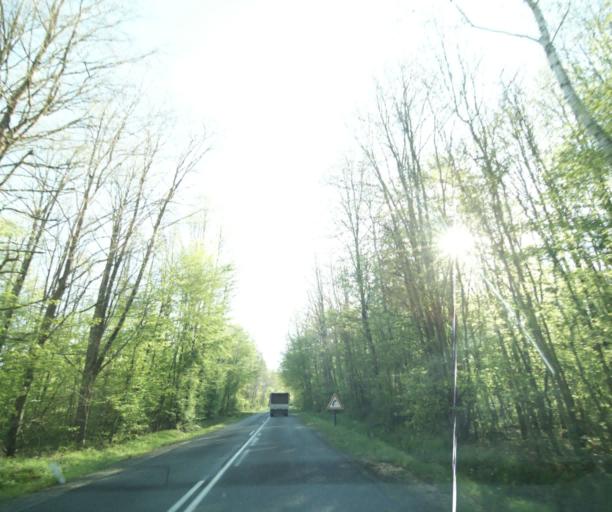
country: FR
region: Ile-de-France
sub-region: Departement de Seine-et-Marne
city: La Chapelle-Gauthier
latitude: 48.4978
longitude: 2.9056
